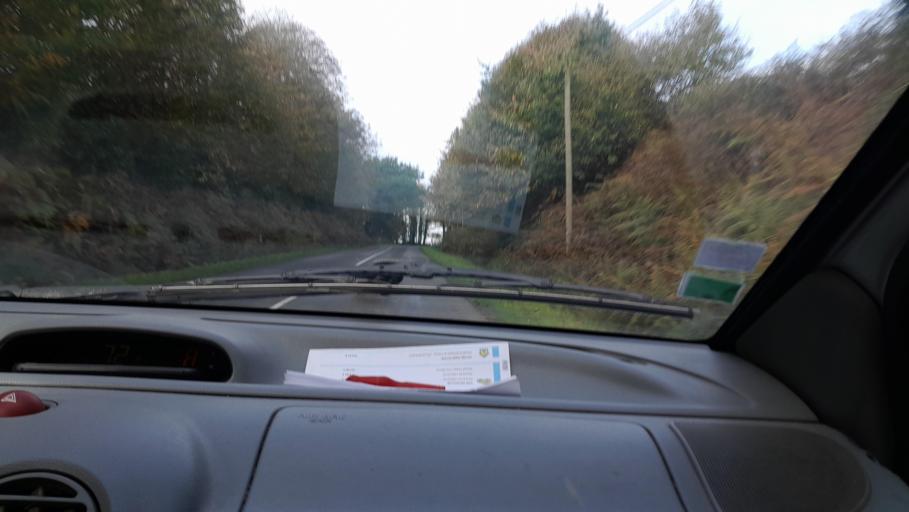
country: FR
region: Brittany
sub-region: Departement d'Ille-et-Vilaine
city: Luitre
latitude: 48.2599
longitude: -1.1299
